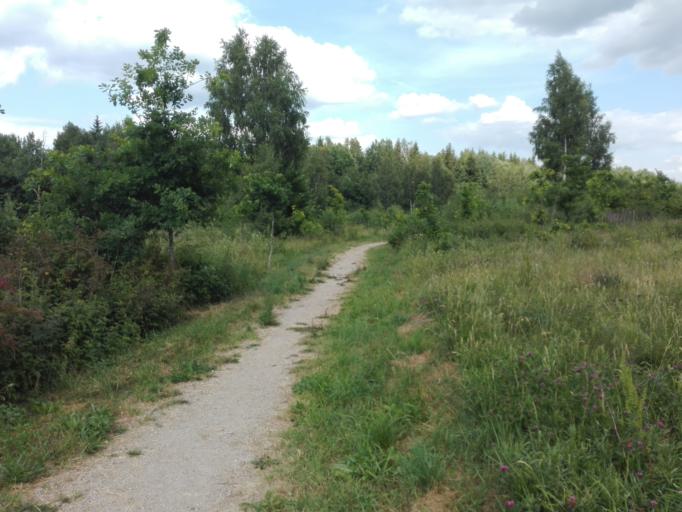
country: LT
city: Skaidiskes
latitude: 54.5319
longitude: 25.6280
